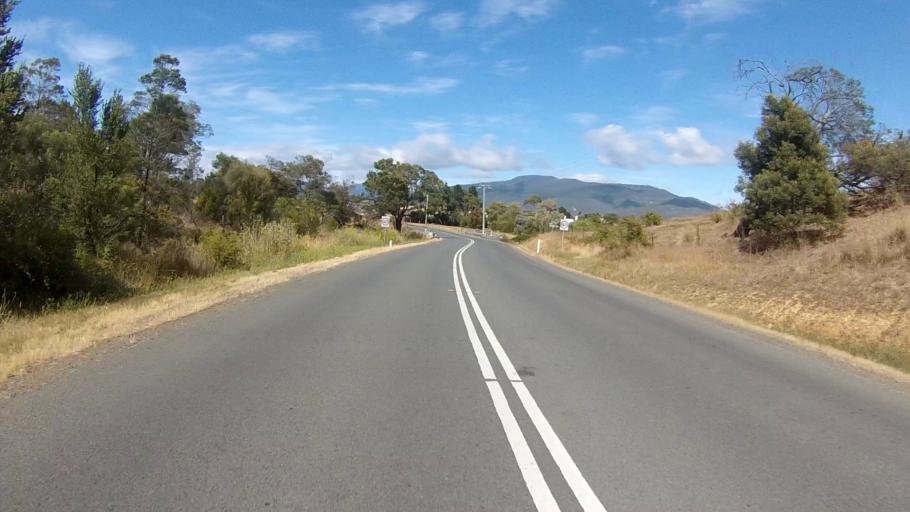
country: AU
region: Tasmania
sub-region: Brighton
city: Old Beach
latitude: -42.7448
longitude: 147.2827
